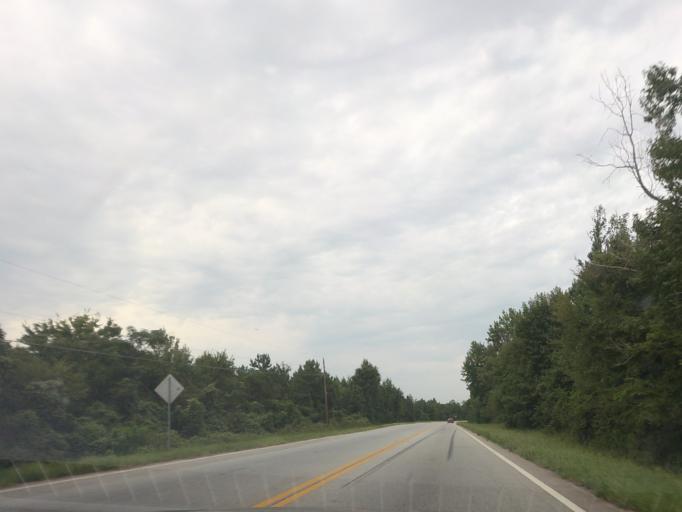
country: US
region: Georgia
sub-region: Bibb County
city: Macon
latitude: 32.7843
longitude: -83.4985
